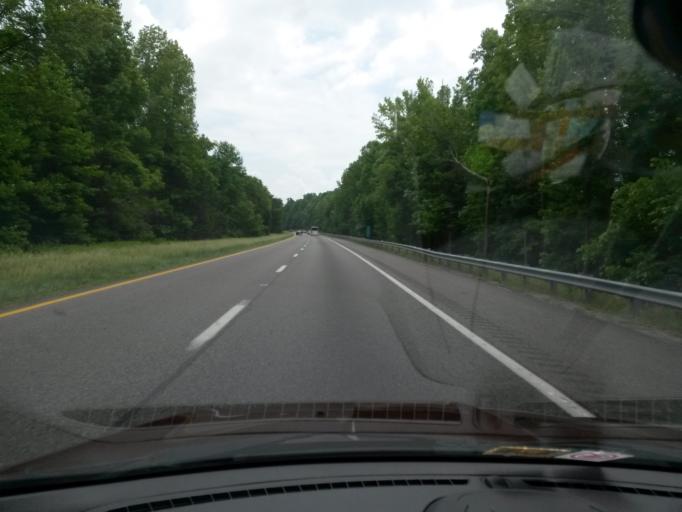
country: US
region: Virginia
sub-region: Goochland County
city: Goochland
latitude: 37.7197
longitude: -77.8127
